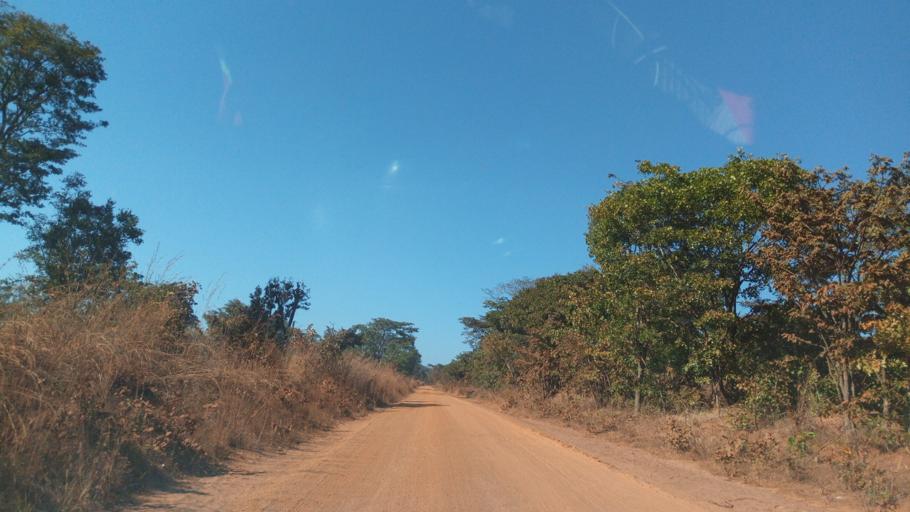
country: ZM
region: Luapula
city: Mwense
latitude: -10.6601
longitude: 28.4076
